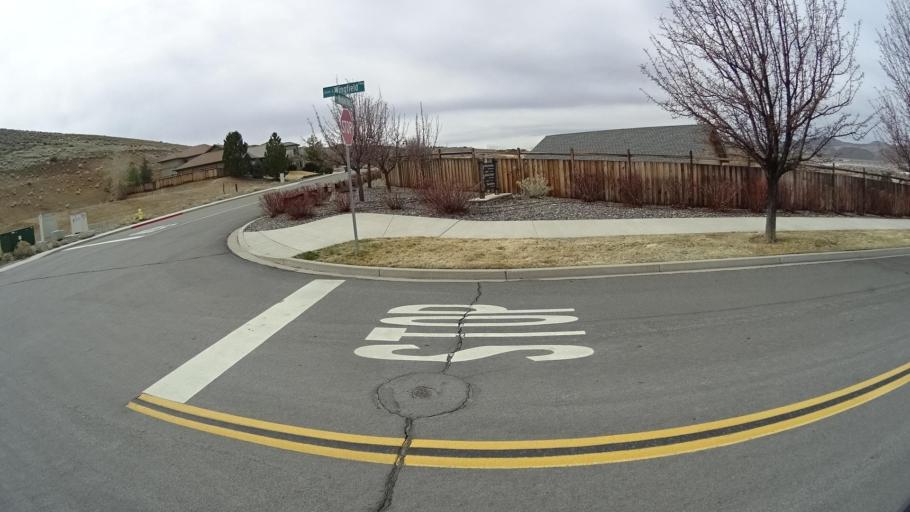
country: US
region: Nevada
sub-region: Washoe County
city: Spanish Springs
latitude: 39.6031
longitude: -119.6862
